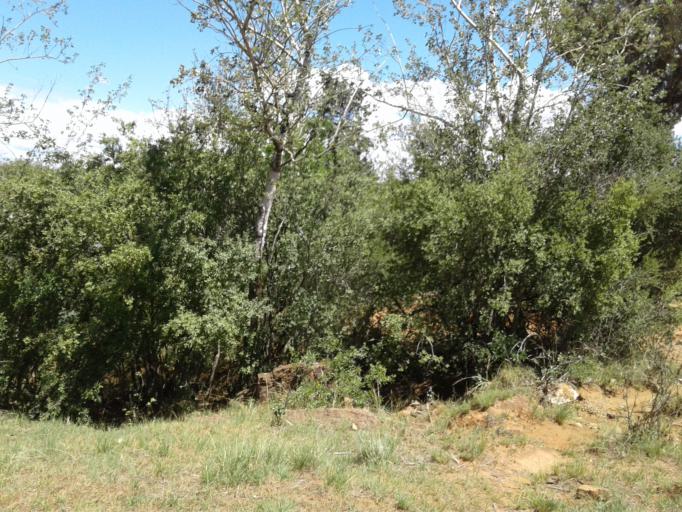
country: LS
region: Quthing
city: Quthing
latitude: -30.3838
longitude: 27.5562
